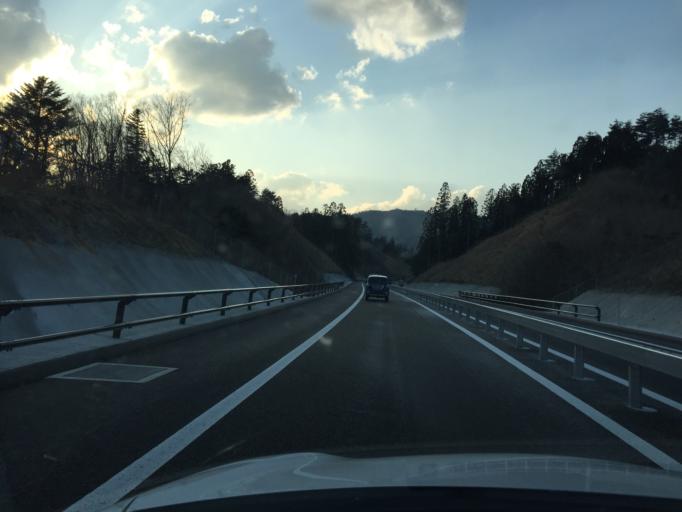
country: JP
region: Miyagi
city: Marumori
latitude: 37.7790
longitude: 140.8310
